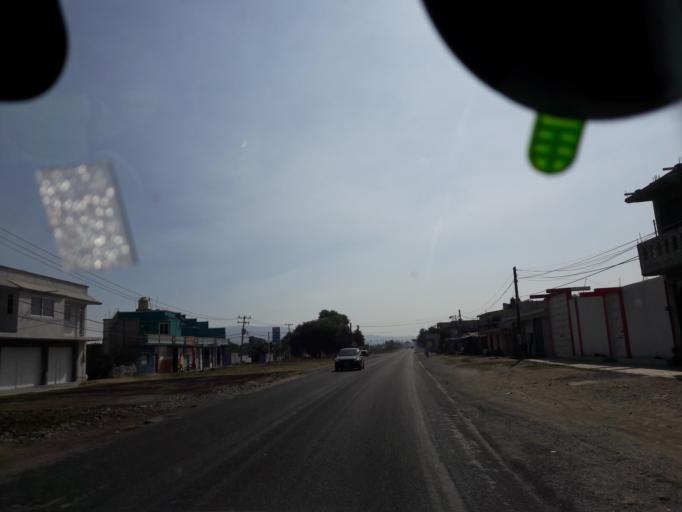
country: MX
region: Tlaxcala
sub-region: Ixtacuixtla de Mariano Matamoros
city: Santa Justina Ecatepec
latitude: 19.3105
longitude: -98.3498
